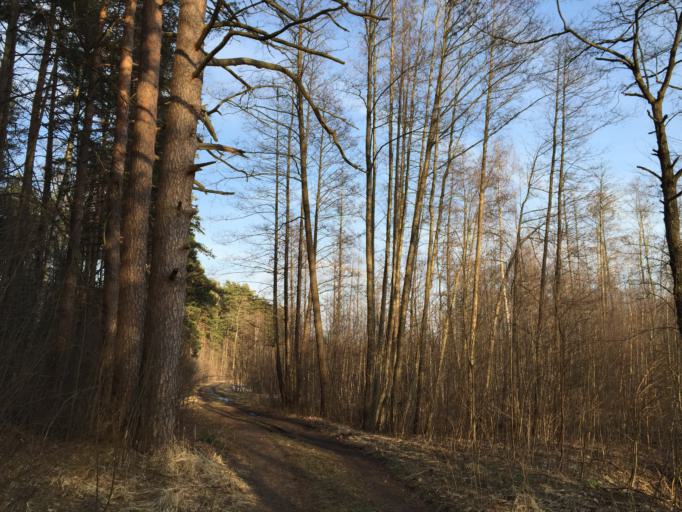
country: LV
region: Stopini
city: Ulbroka
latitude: 56.9608
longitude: 24.2835
